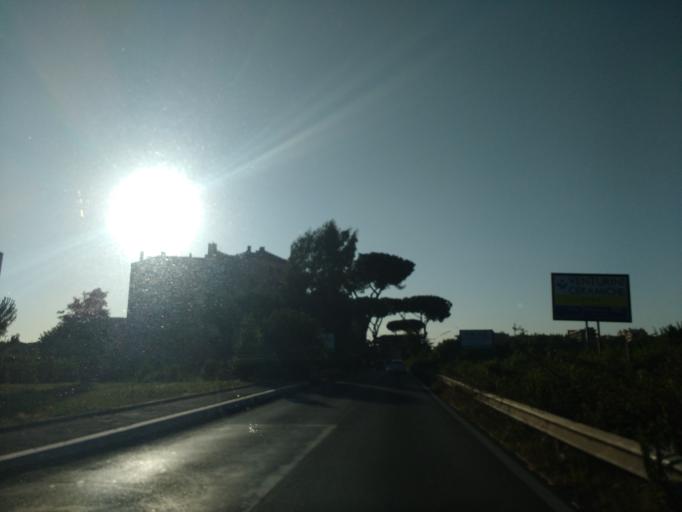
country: IT
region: Latium
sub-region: Citta metropolitana di Roma Capitale
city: Vitinia
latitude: 41.7676
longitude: 12.3787
